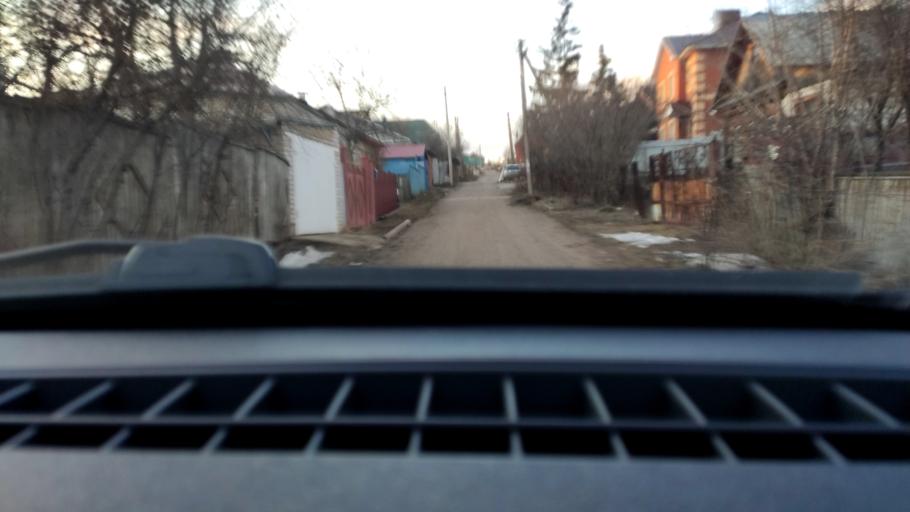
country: RU
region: Bashkortostan
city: Mikhaylovka
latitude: 54.8063
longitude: 55.8863
